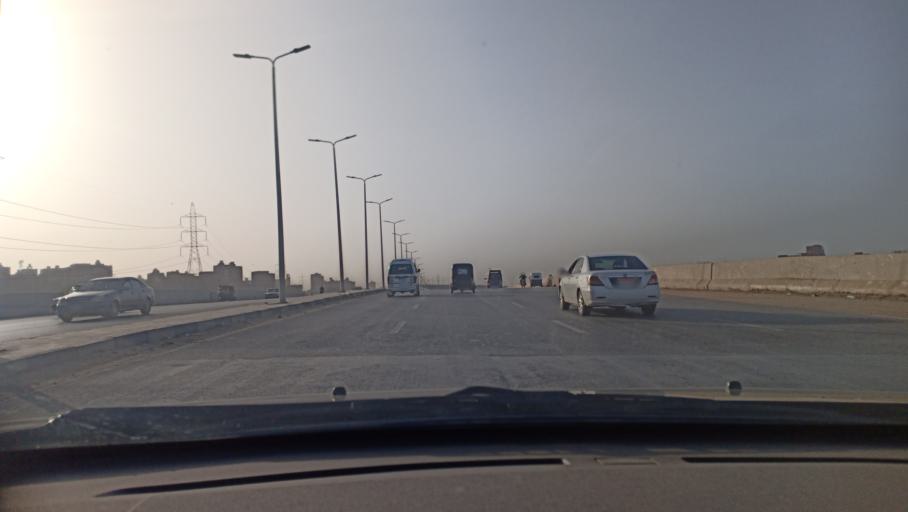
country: EG
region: Muhafazat al Qalyubiyah
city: Qalyub
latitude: 30.1427
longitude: 31.2625
